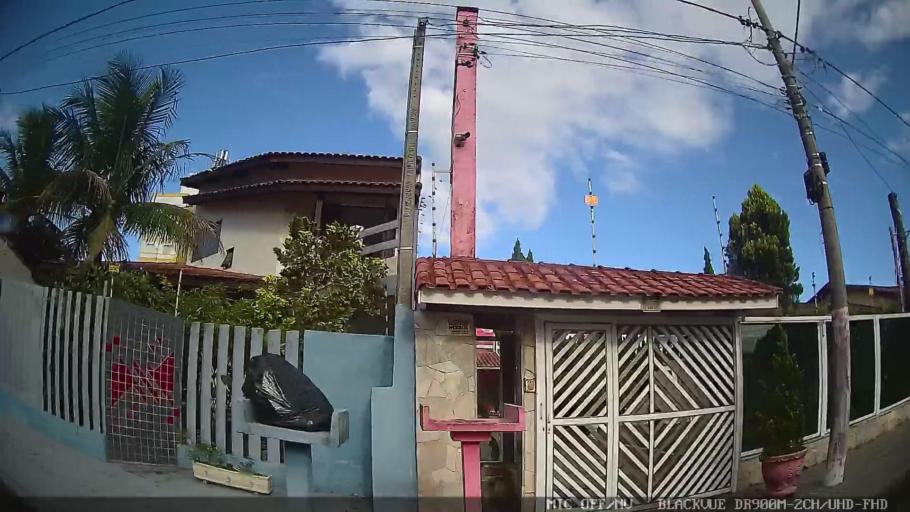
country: BR
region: Sao Paulo
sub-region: Itanhaem
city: Itanhaem
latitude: -24.2136
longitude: -46.8419
